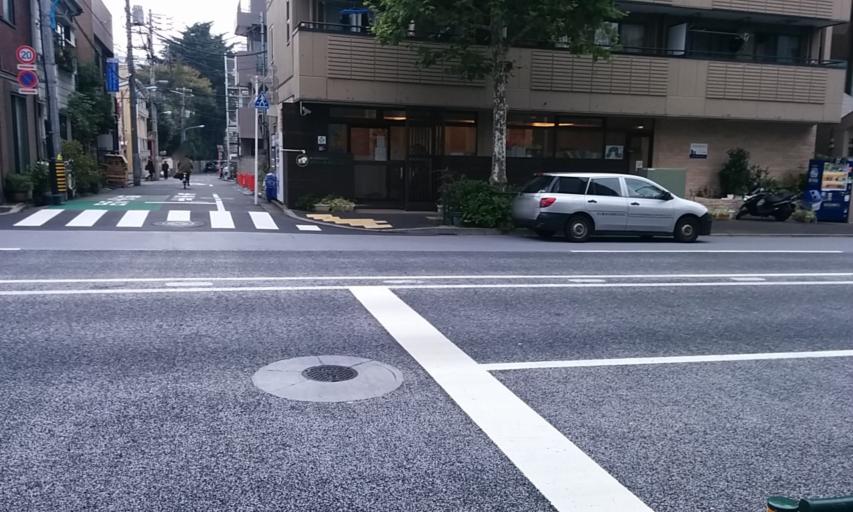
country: JP
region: Tokyo
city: Tokyo
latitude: 35.7049
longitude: 139.7286
